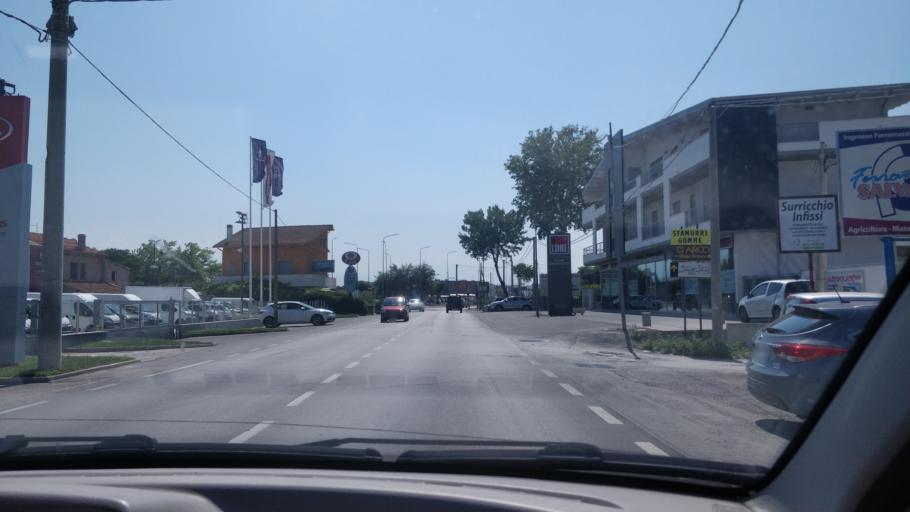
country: IT
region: Abruzzo
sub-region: Provincia di Chieti
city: Sambuceto
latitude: 42.4173
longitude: 14.1724
